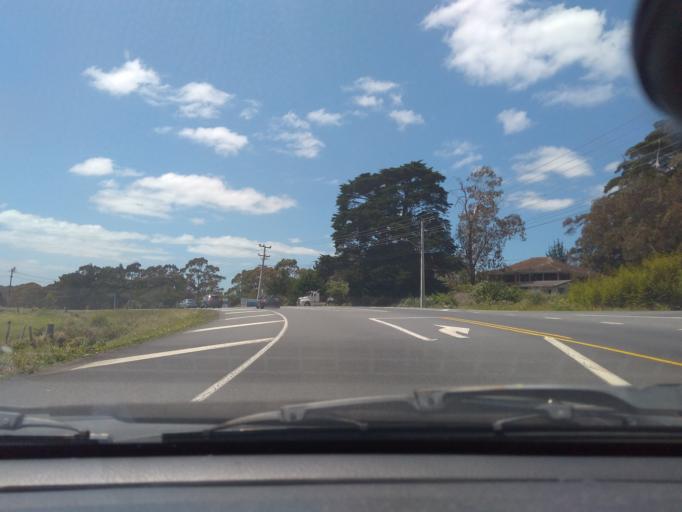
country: NZ
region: Auckland
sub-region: Auckland
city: Pakuranga
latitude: -36.9392
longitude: 174.9878
